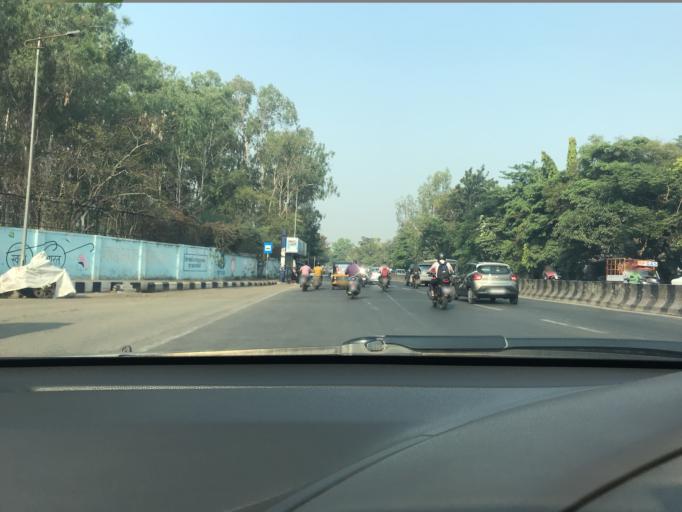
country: IN
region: Maharashtra
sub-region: Pune Division
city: Khadki
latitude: 18.5480
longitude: 73.8145
